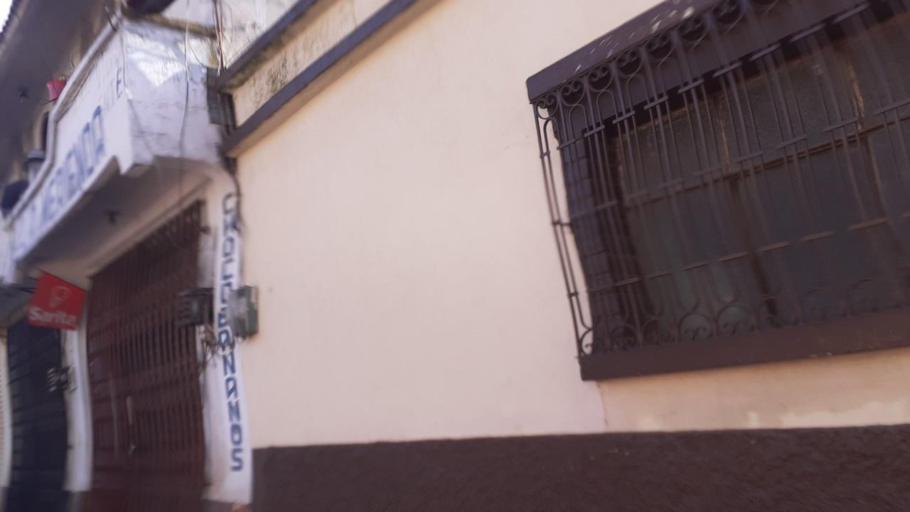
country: GT
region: Quetzaltenango
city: Ostuncalco
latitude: 14.8673
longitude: -91.6213
